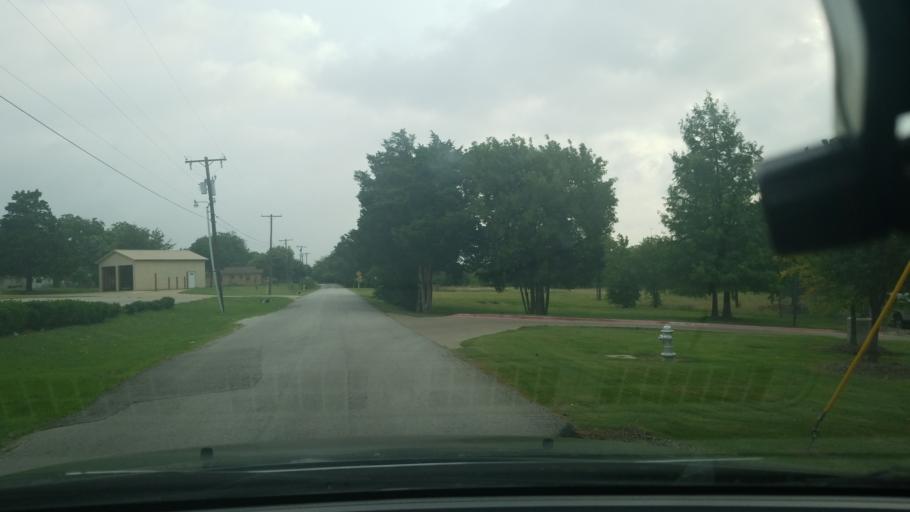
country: US
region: Texas
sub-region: Dallas County
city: Mesquite
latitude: 32.7866
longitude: -96.6298
